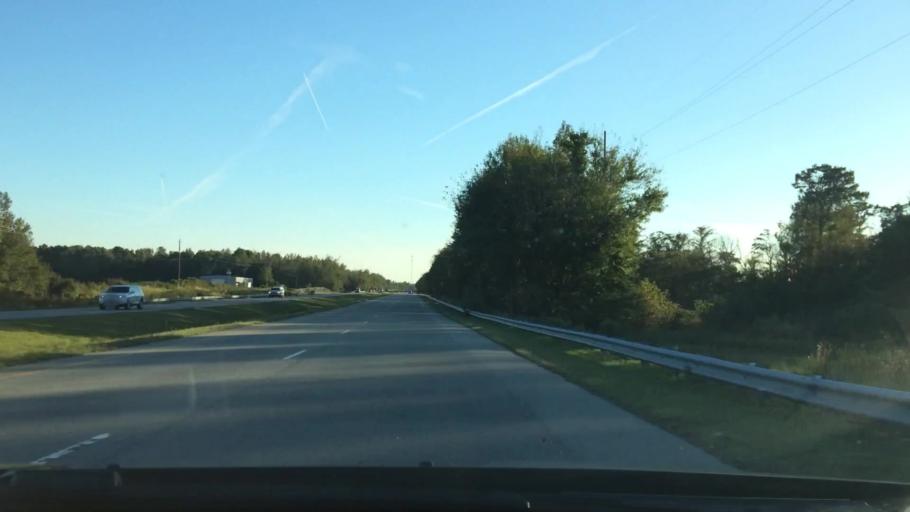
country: US
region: North Carolina
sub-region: Pitt County
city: Grifton
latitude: 35.3910
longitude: -77.4464
